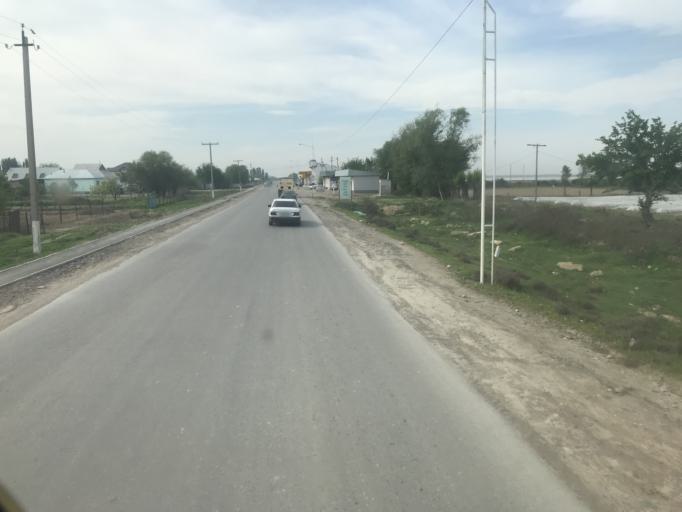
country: KZ
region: Ongtustik Qazaqstan
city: Asykata
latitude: 41.0042
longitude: 68.2144
